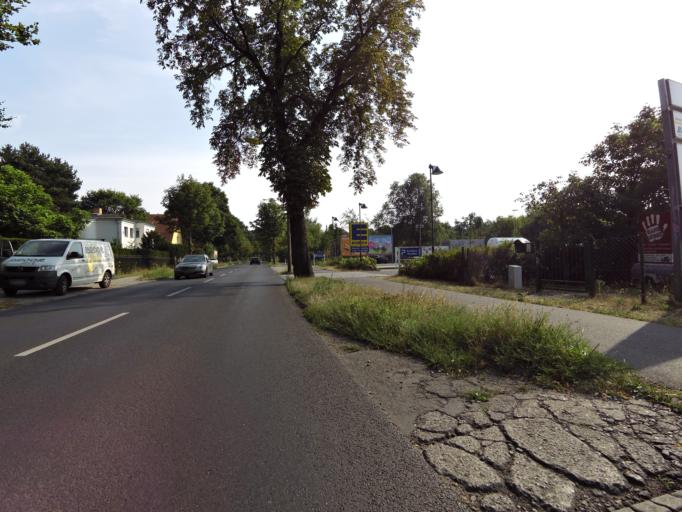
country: DE
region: Berlin
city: Grunau
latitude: 52.4094
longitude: 13.5732
